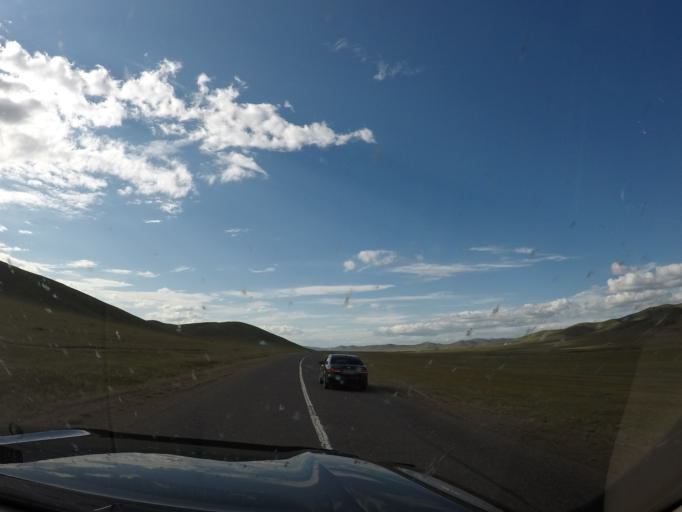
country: MN
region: Hentiy
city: Modot
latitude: 47.6944
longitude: 109.0851
